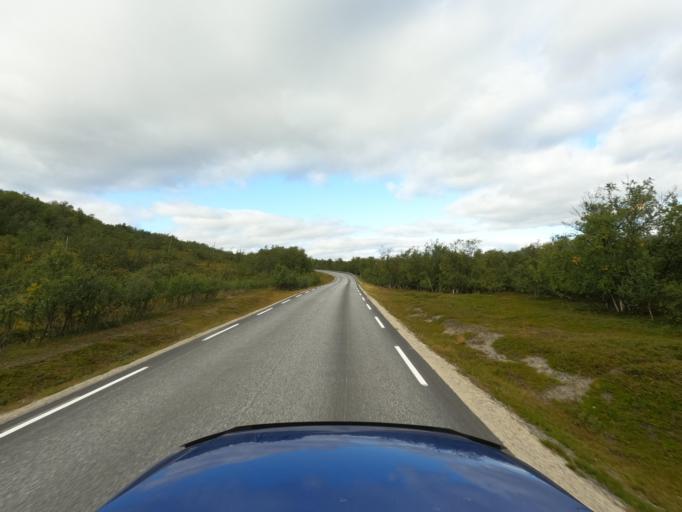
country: NO
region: Finnmark Fylke
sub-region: Porsanger
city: Lakselv
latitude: 70.1510
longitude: 24.8986
